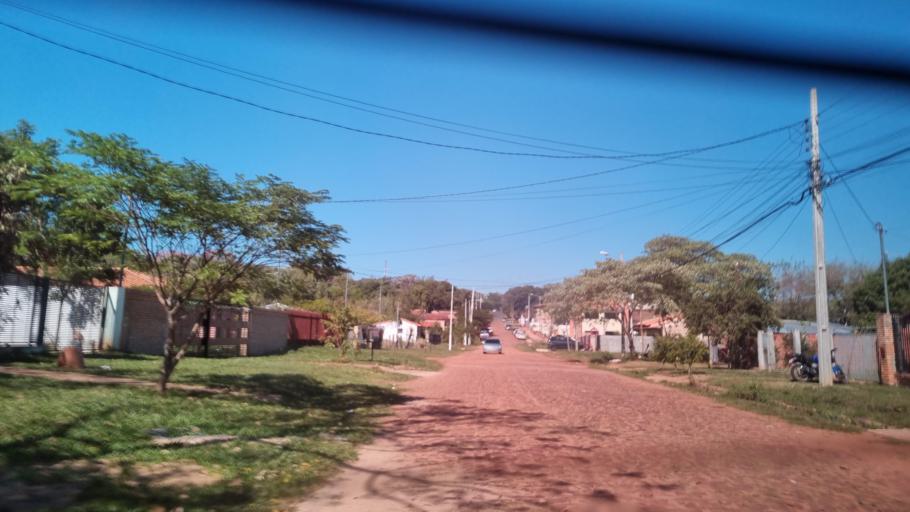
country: PY
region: Misiones
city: San Juan Bautista
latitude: -26.6627
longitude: -57.1406
